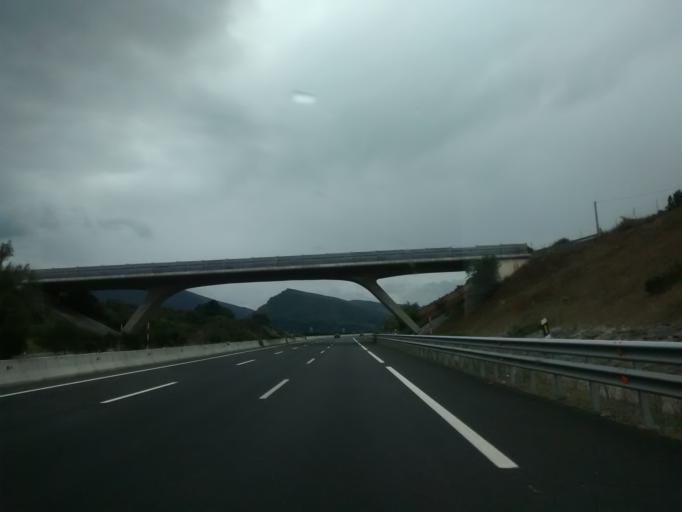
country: ES
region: Cantabria
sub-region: Provincia de Cantabria
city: Molledo
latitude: 43.1460
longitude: -4.0557
